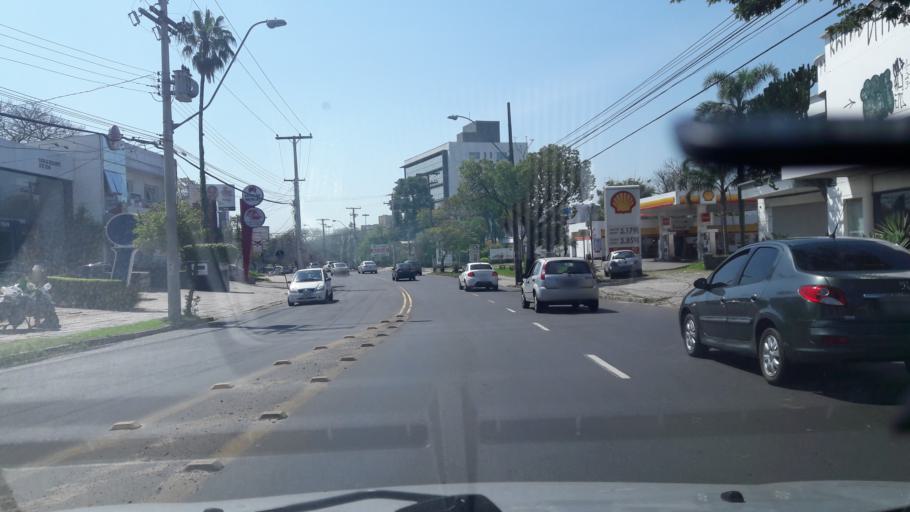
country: BR
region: Rio Grande do Sul
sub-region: Porto Alegre
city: Porto Alegre
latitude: -30.1032
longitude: -51.2515
